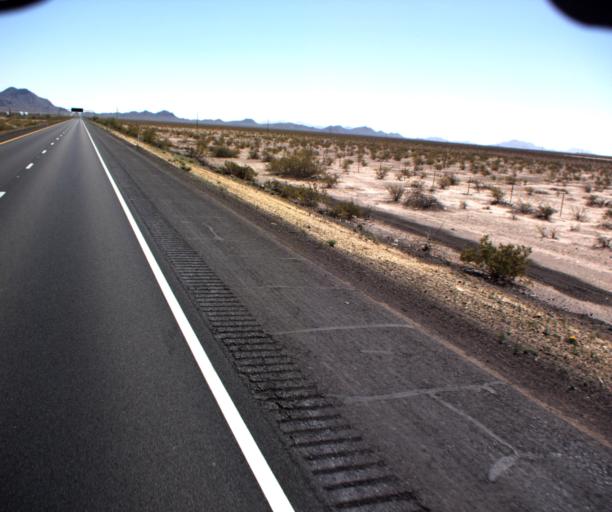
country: US
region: Arizona
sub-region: La Paz County
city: Salome
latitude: 33.6212
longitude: -113.7037
